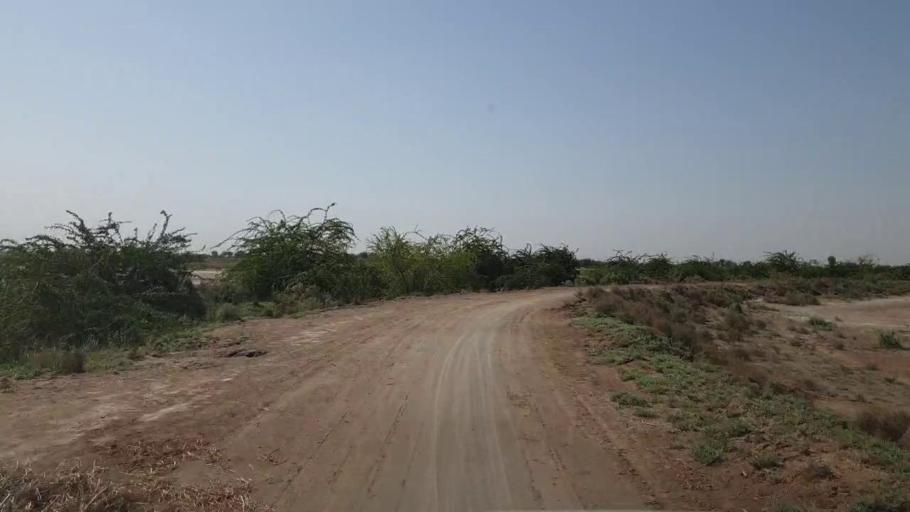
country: PK
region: Sindh
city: Tando Bago
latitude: 24.7397
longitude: 69.0252
